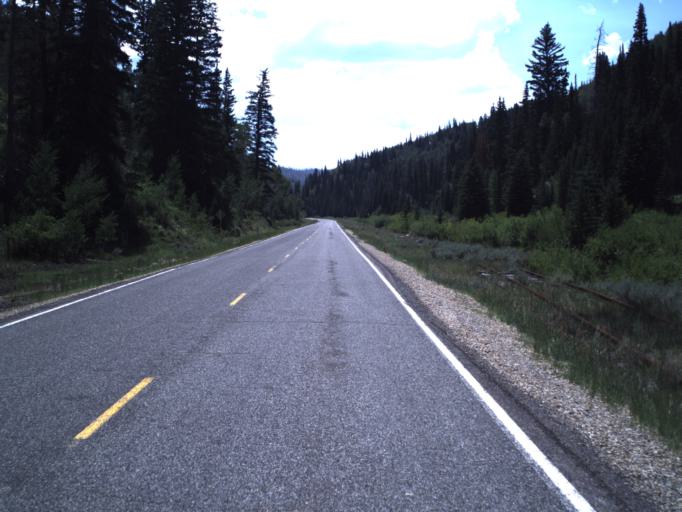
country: US
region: Utah
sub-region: Sanpete County
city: Fairview
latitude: 39.6619
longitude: -111.1556
